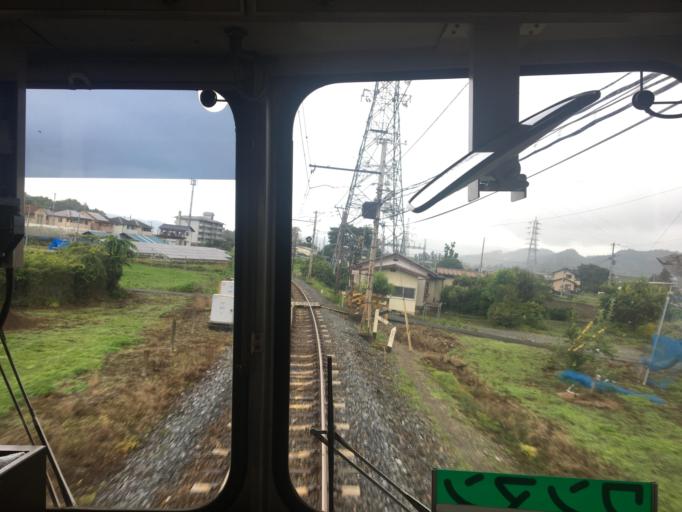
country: JP
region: Saitama
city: Chichibu
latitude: 35.9614
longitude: 139.0430
